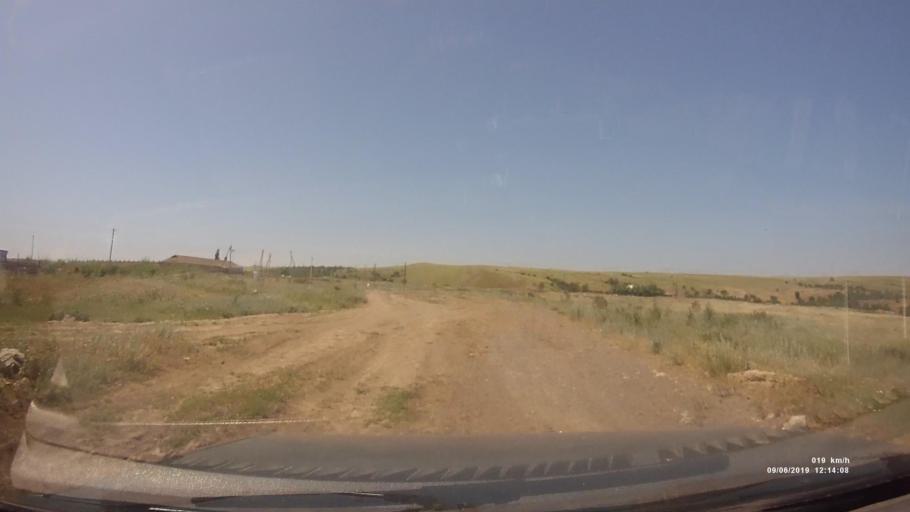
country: RU
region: Rostov
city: Staraya Stanitsa
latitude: 48.2515
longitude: 40.3252
